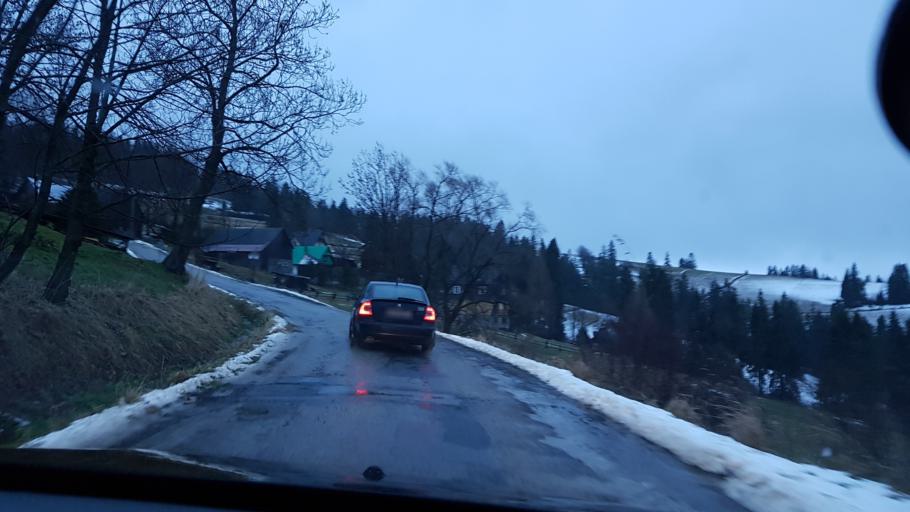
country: PL
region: Lesser Poland Voivodeship
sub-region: Powiat tatrzanski
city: Czarna Gora
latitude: 49.3582
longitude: 20.1611
